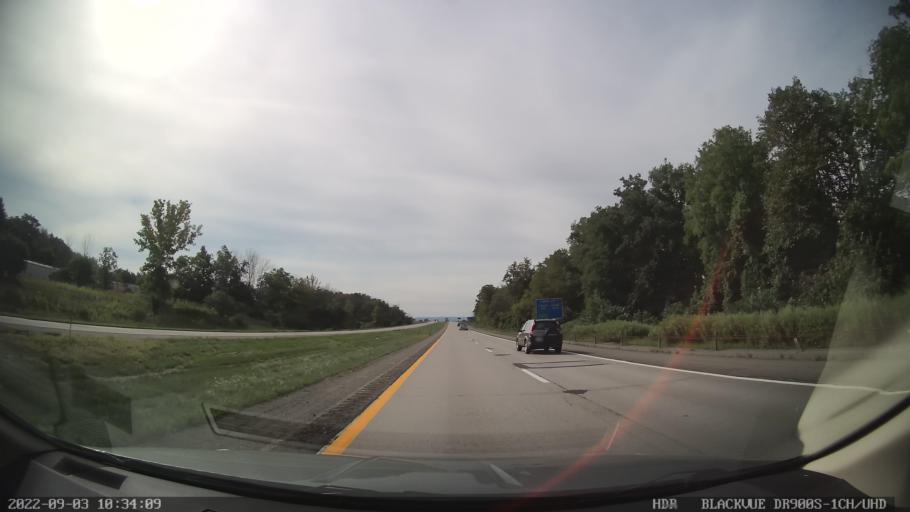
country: US
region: New York
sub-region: Livingston County
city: Mount Morris
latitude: 42.7439
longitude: -77.8398
